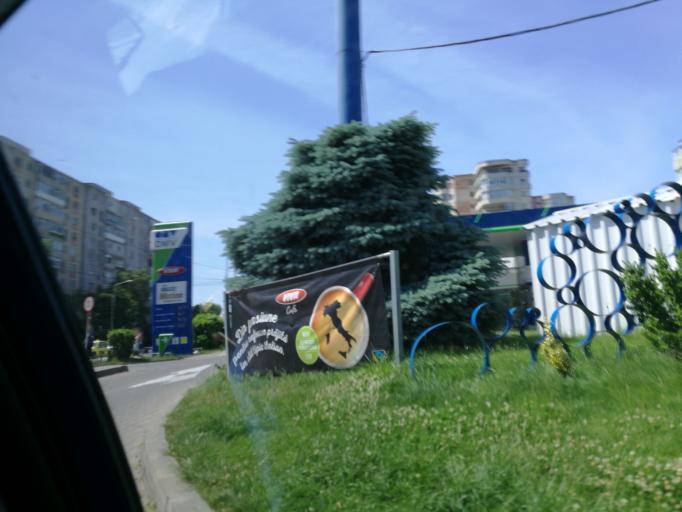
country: RO
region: Constanta
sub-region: Municipiul Constanta
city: Constanta
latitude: 44.2034
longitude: 28.6230
